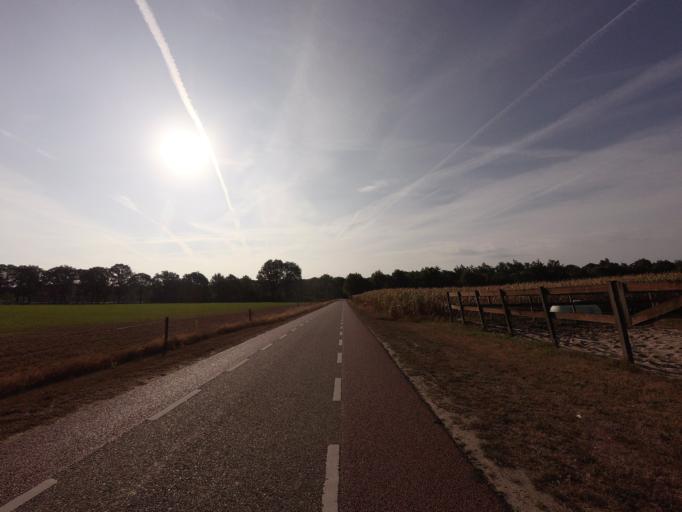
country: NL
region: North Brabant
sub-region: Gemeente Landerd
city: Zeeland
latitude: 51.6772
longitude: 5.7015
